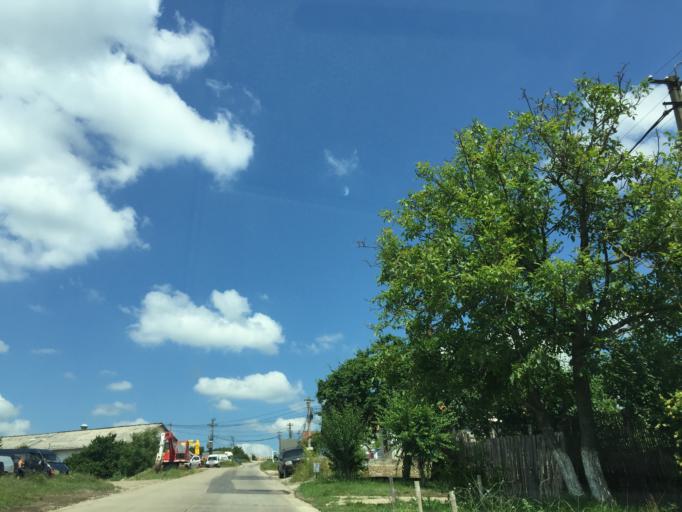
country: RO
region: Cluj
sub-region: Comuna Baciu
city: Baciu
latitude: 46.7878
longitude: 23.5586
